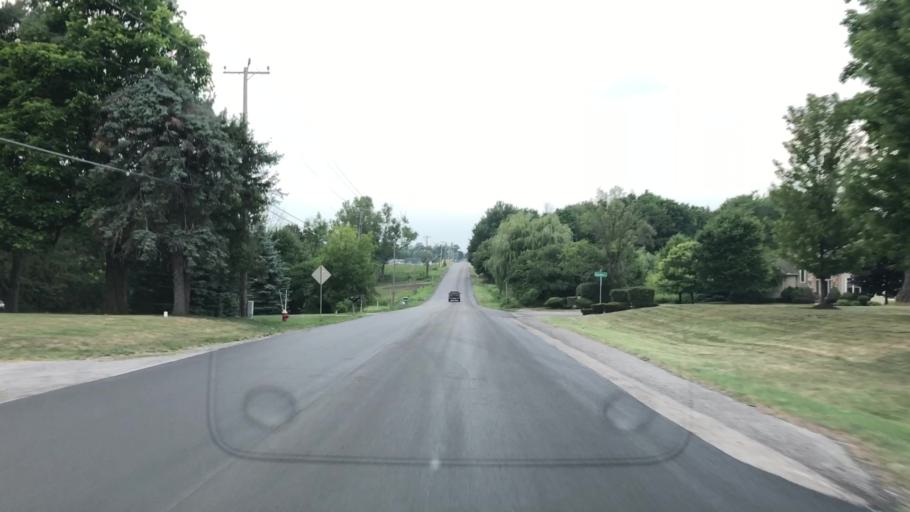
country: US
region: New York
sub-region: Erie County
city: Elma Center
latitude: 42.8285
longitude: -78.6059
